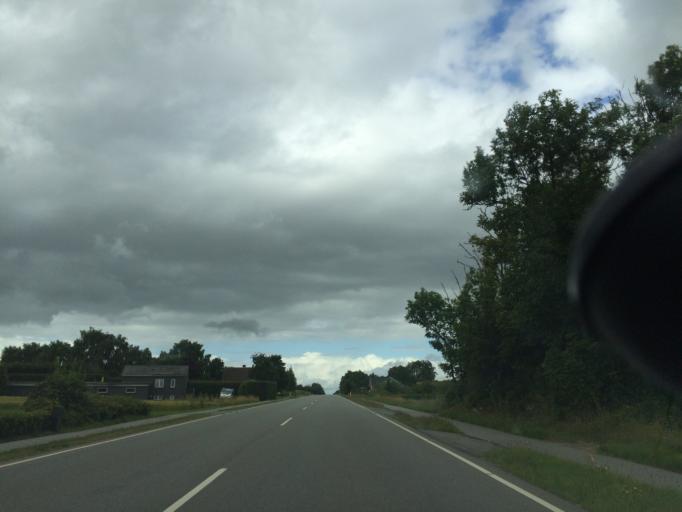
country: DK
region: Central Jutland
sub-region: Skanderborg Kommune
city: Galten
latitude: 56.1484
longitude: 9.8774
